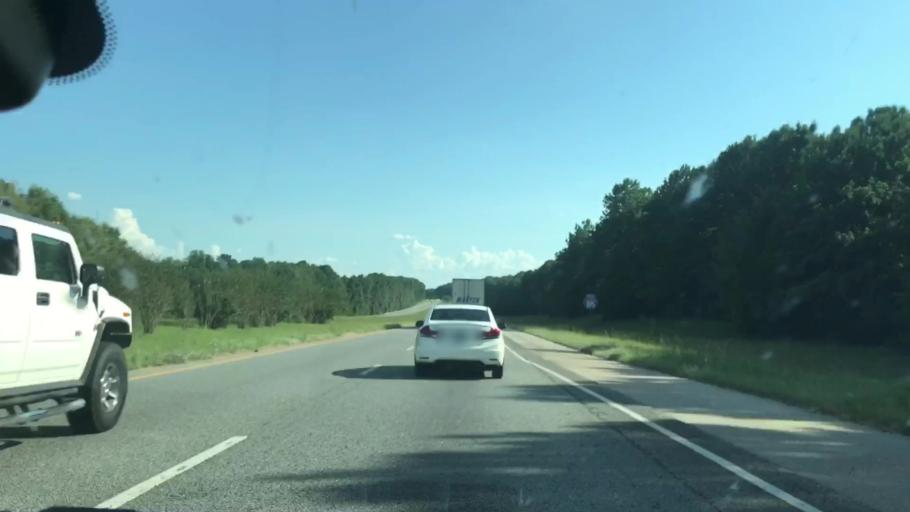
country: US
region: Georgia
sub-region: Troup County
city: La Grange
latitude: 32.9545
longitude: -84.9567
